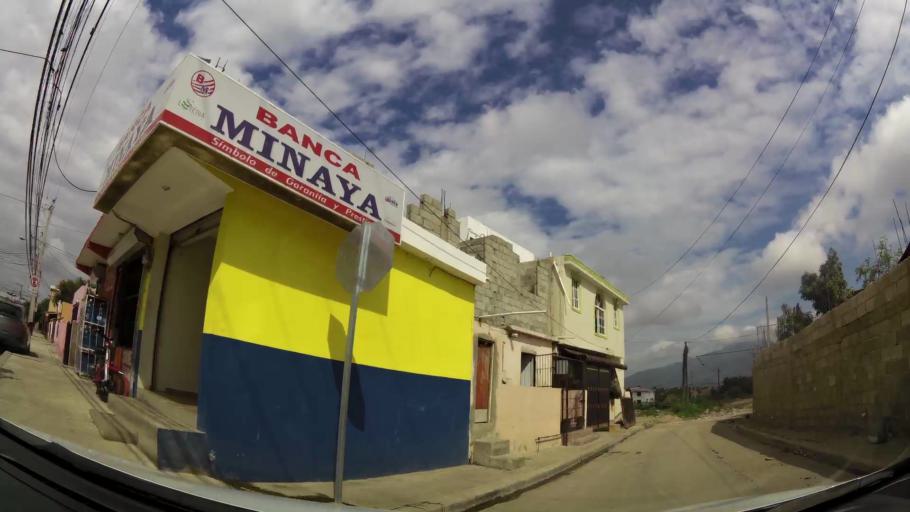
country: DO
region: Santiago
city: Santiago de los Caballeros
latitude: 19.4887
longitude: -70.7305
